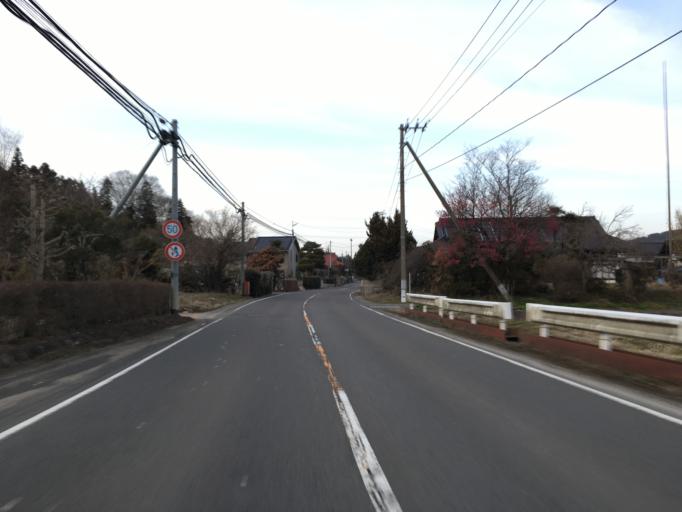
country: JP
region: Ibaraki
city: Daigo
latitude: 36.9205
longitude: 140.4078
